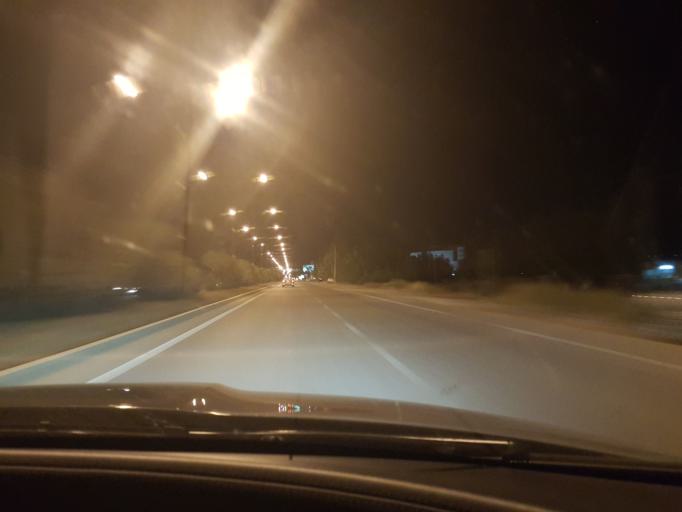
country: IQ
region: Arbil
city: Erbil
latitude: 36.2725
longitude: 44.0978
